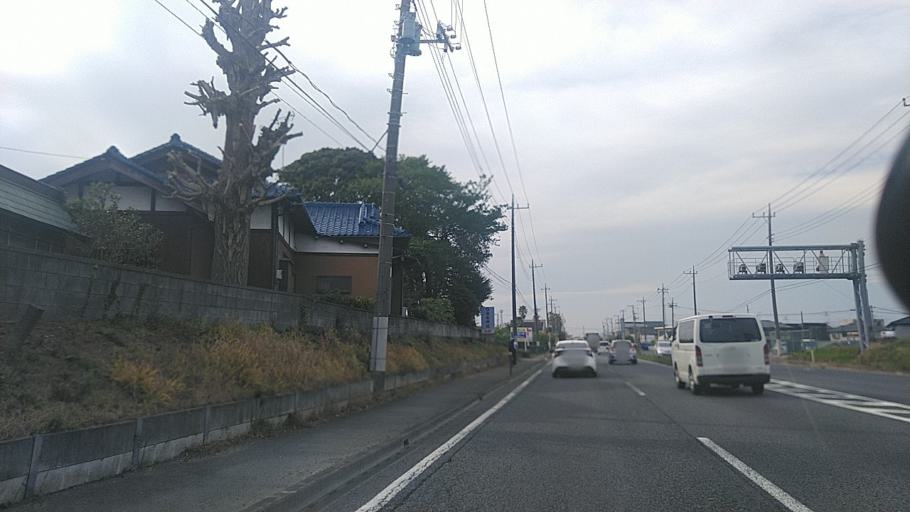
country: JP
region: Chiba
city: Shiroi
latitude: 35.7488
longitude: 140.1177
